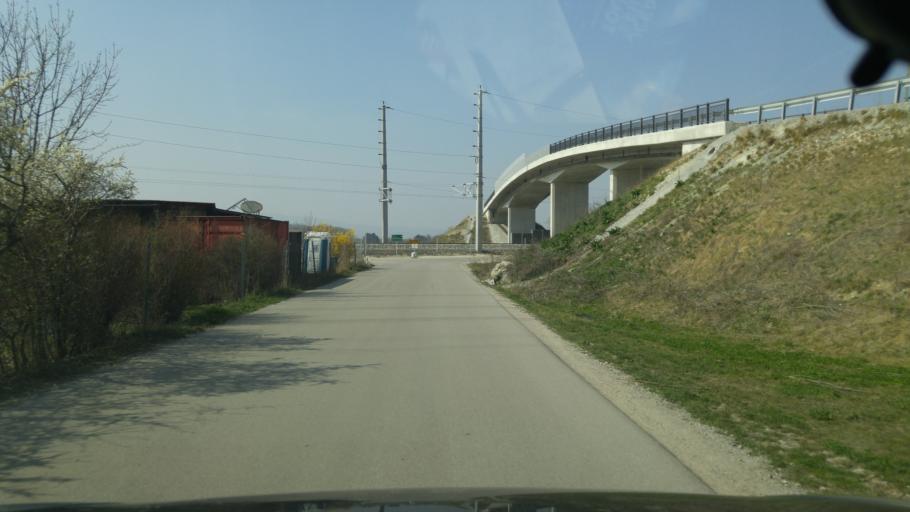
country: AT
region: Lower Austria
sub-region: Politischer Bezirk Modling
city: Munchendorf
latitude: 48.0193
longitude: 16.3871
